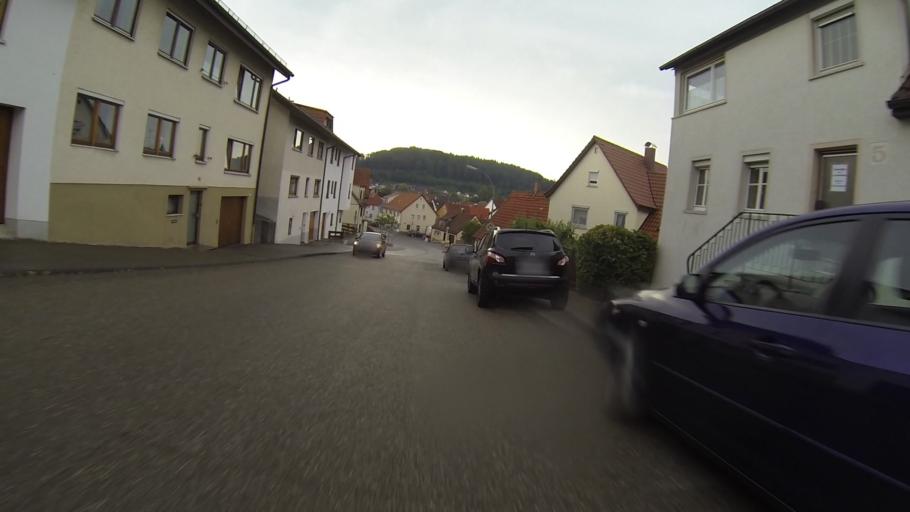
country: DE
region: Baden-Wuerttemberg
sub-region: Regierungsbezirk Stuttgart
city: Heidenheim an der Brenz
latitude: 48.7070
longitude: 10.1662
